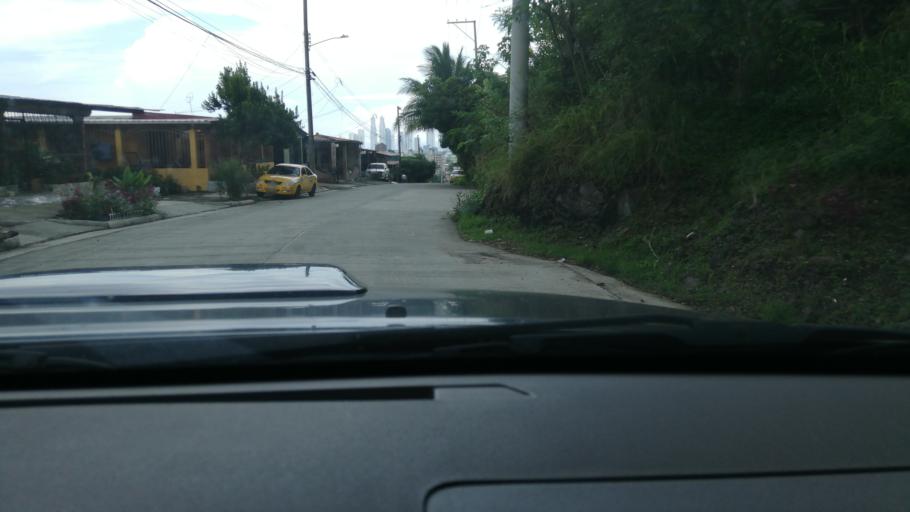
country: PA
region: Panama
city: San Miguelito
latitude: 9.0513
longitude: -79.4778
